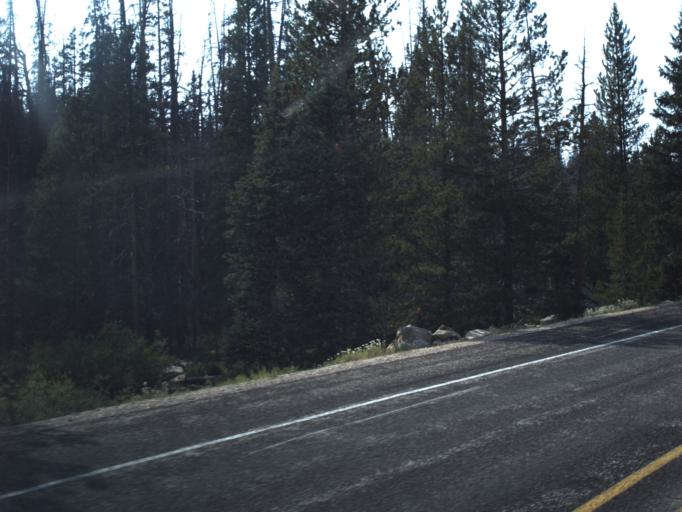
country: US
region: Utah
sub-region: Summit County
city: Kamas
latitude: 40.6757
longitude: -110.9535
